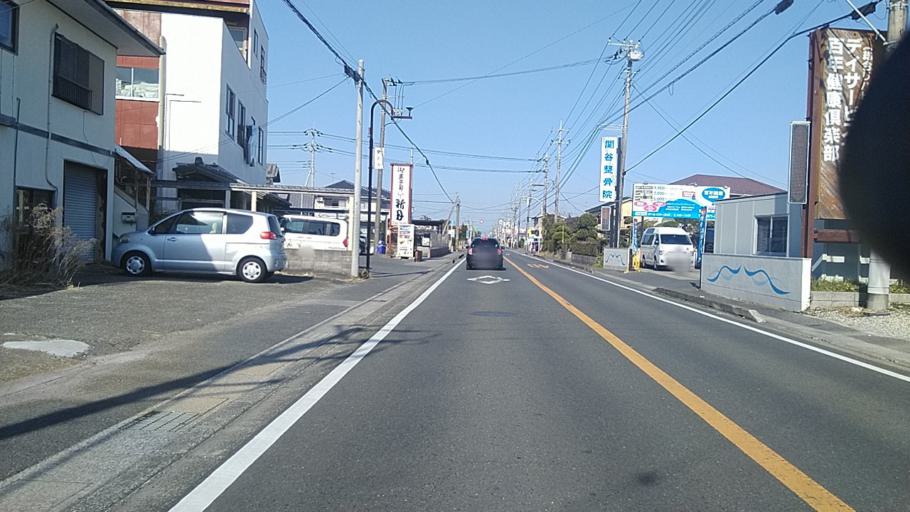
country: JP
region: Chiba
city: Mobara
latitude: 35.4405
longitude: 140.2946
